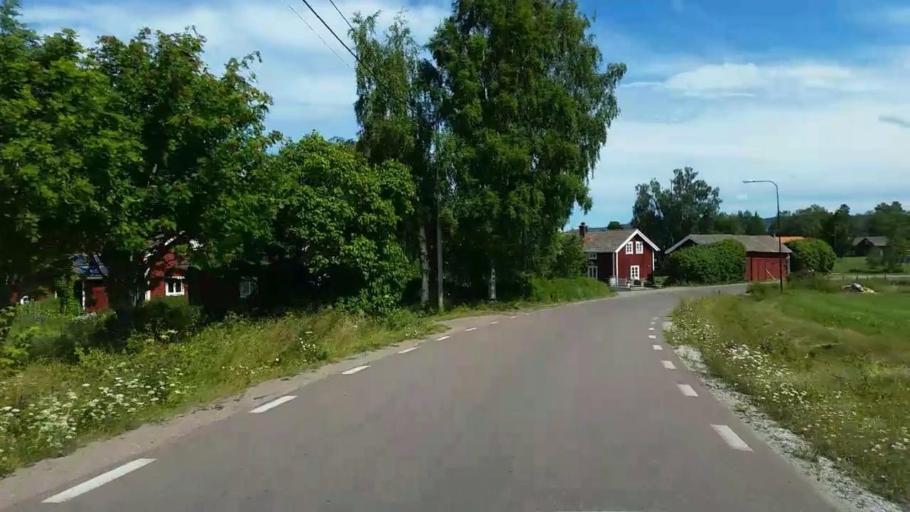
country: SE
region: Dalarna
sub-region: Rattviks Kommun
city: Vikarbyn
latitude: 60.8390
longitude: 15.0049
